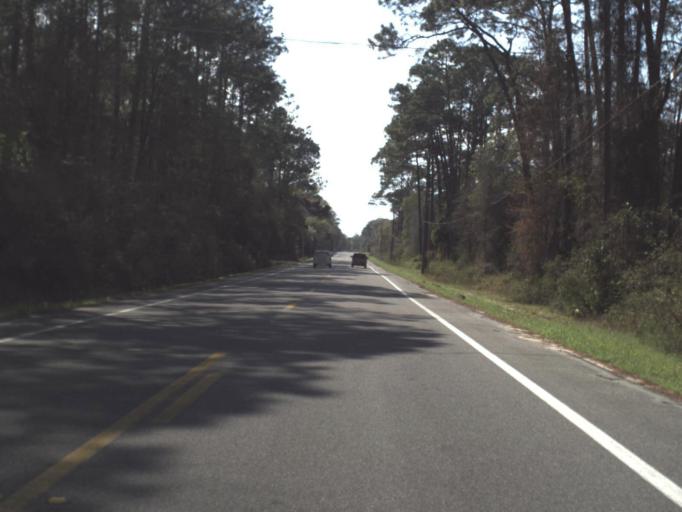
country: US
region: Florida
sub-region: Wakulla County
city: Crawfordville
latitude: 30.0769
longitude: -84.4202
